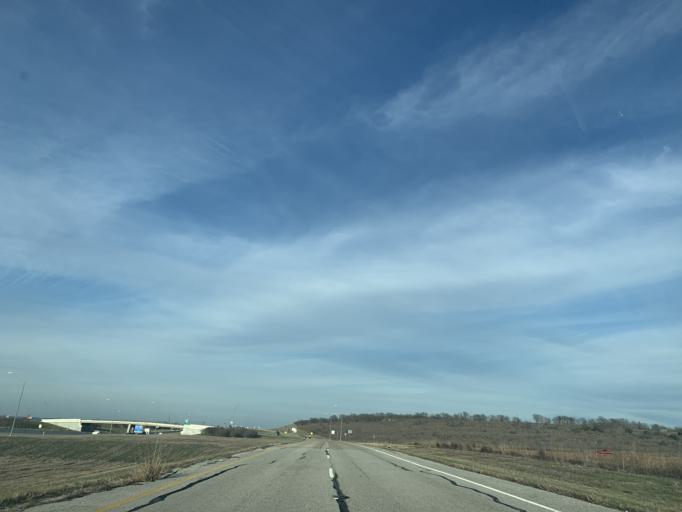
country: US
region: Texas
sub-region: Bell County
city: Salado
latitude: 30.8851
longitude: -97.5744
